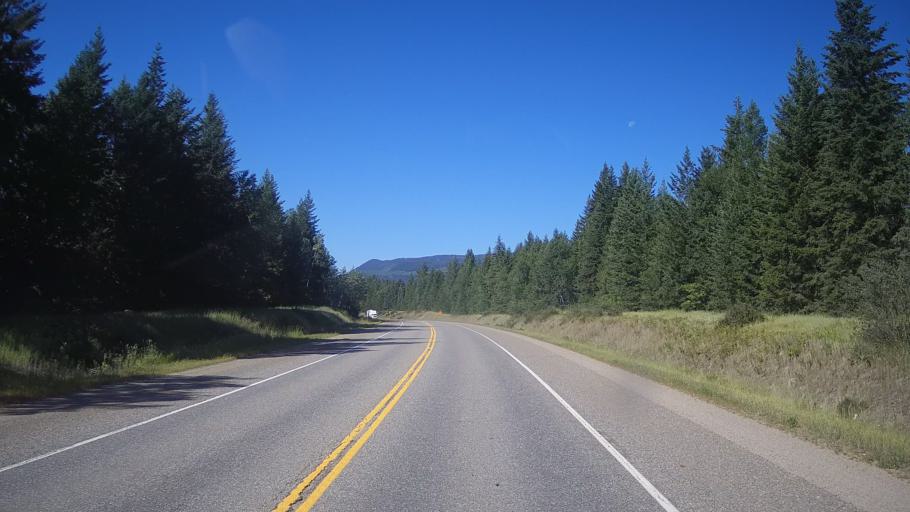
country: CA
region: British Columbia
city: Chase
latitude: 51.6357
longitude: -120.0858
